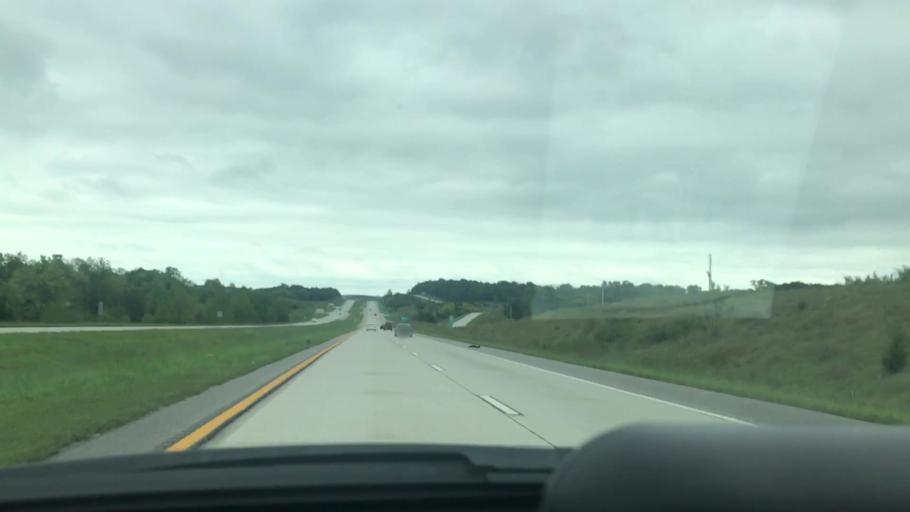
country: US
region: Missouri
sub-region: Greene County
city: Fair Grove
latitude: 37.5111
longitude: -93.1387
